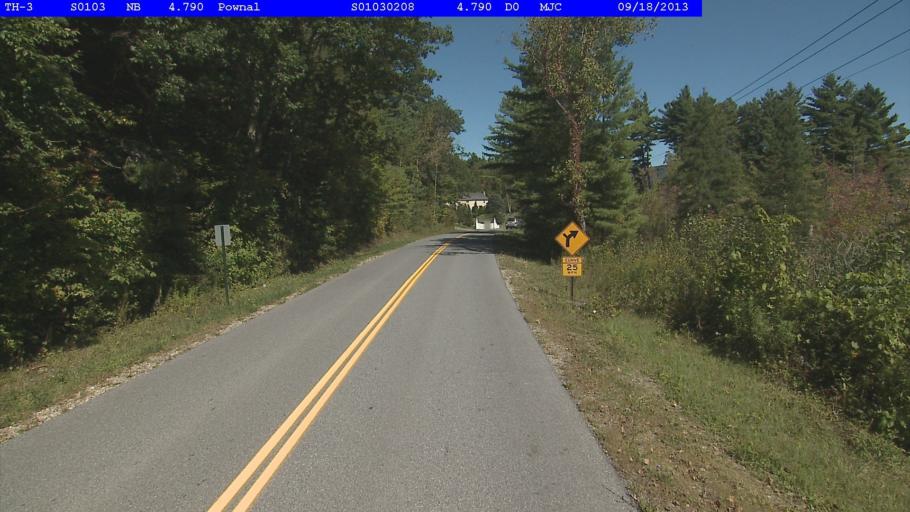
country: US
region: Vermont
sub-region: Bennington County
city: Bennington
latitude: 42.8008
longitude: -73.1895
